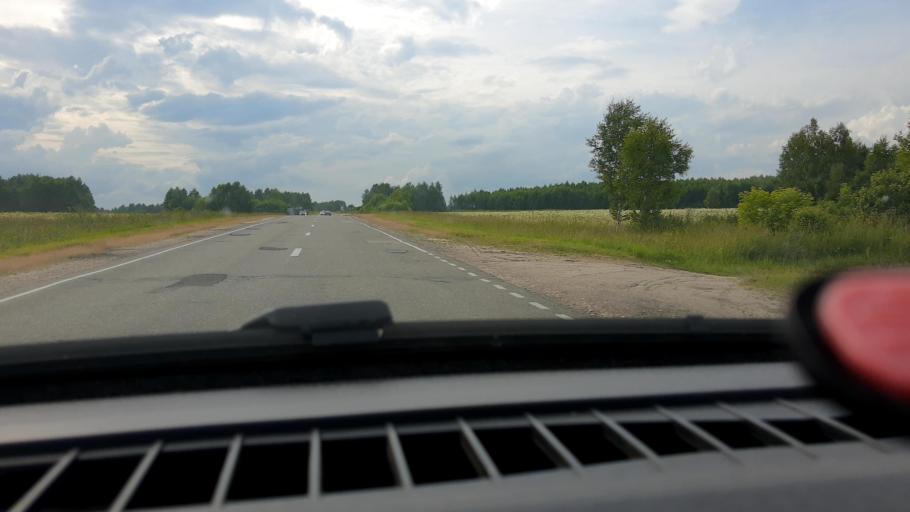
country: RU
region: Nizjnij Novgorod
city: Neklyudovo
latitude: 56.5041
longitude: 43.9798
